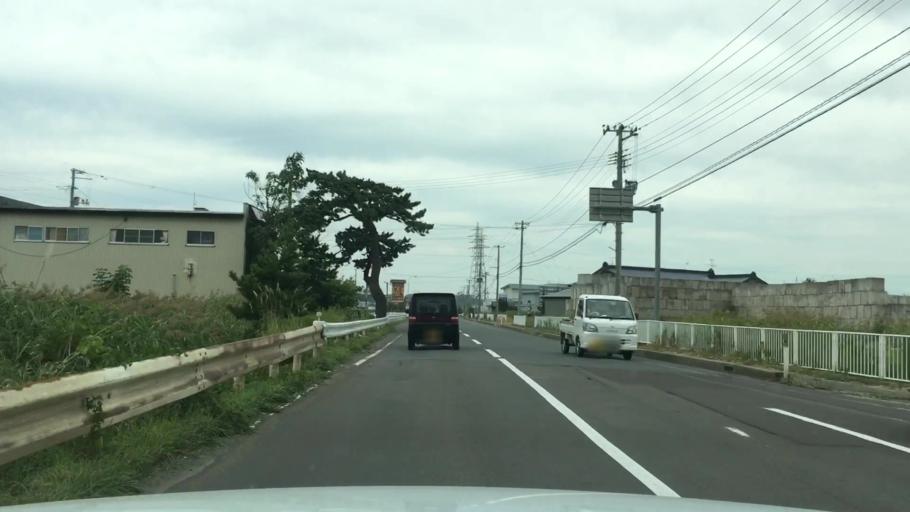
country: JP
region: Aomori
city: Hirosaki
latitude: 40.6314
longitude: 140.4519
